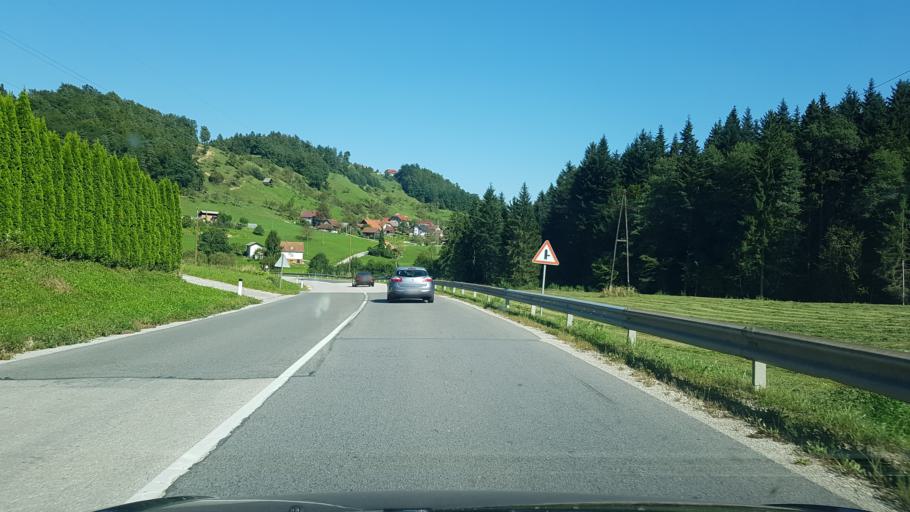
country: SI
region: Sostanj
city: Sostanj
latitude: 46.3626
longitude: 15.0641
